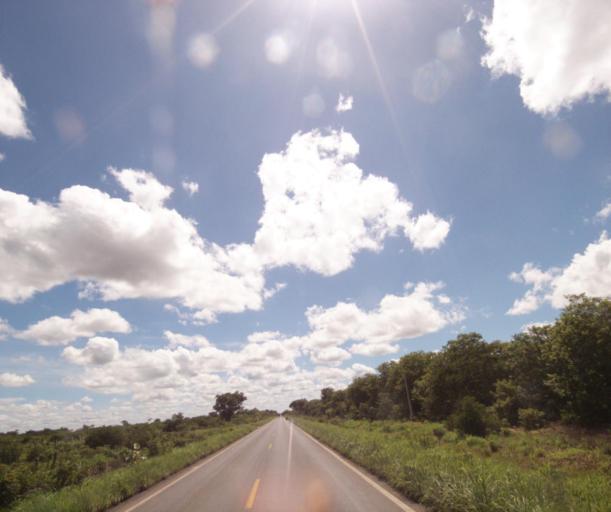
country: BR
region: Bahia
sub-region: Sao Felix Do Coribe
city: Santa Maria da Vitoria
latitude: -13.3897
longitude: -44.1033
